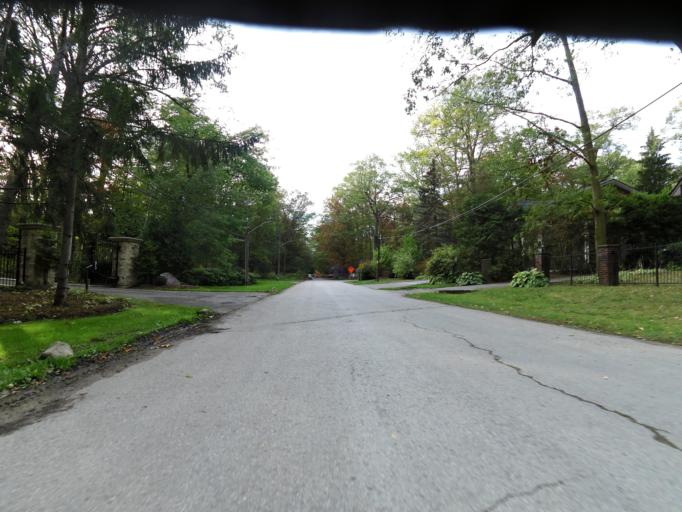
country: CA
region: Ontario
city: Mississauga
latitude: 43.5678
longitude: -79.6068
